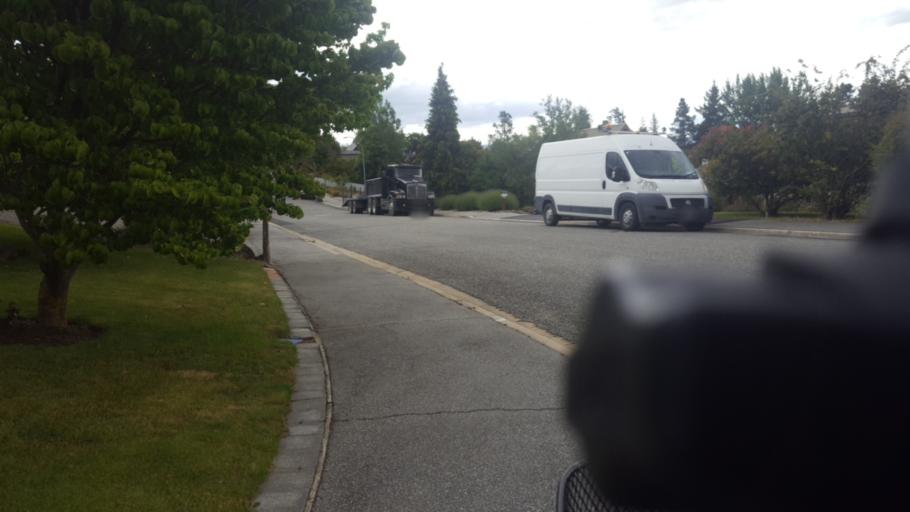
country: NZ
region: Otago
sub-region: Queenstown-Lakes District
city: Wanaka
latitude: -45.2630
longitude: 169.3811
